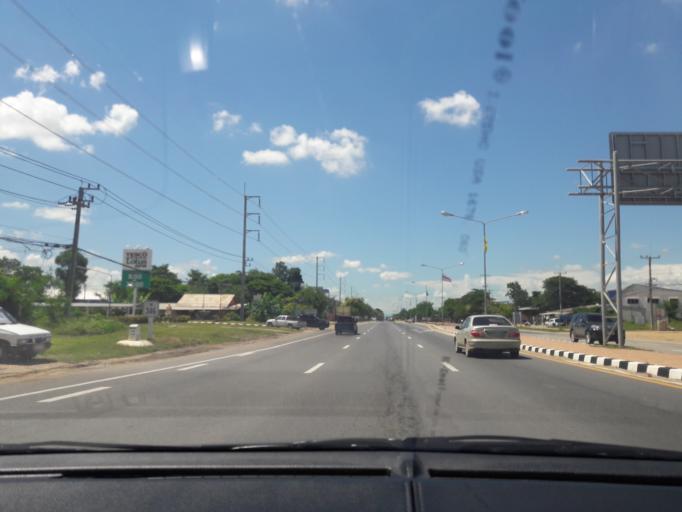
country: TH
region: Kanchanaburi
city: Tha Maka
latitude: 14.0397
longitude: 99.7897
